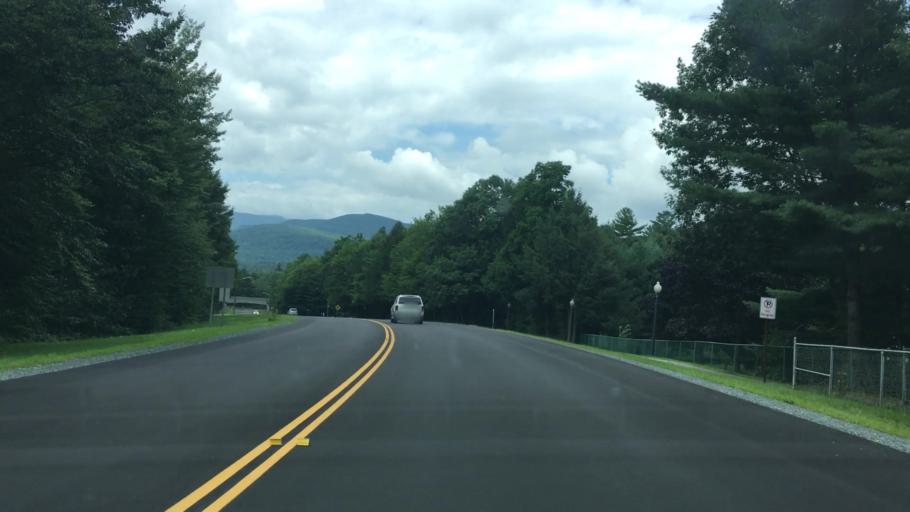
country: US
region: New Hampshire
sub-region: Grafton County
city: Woodstock
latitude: 44.0416
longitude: -71.6758
